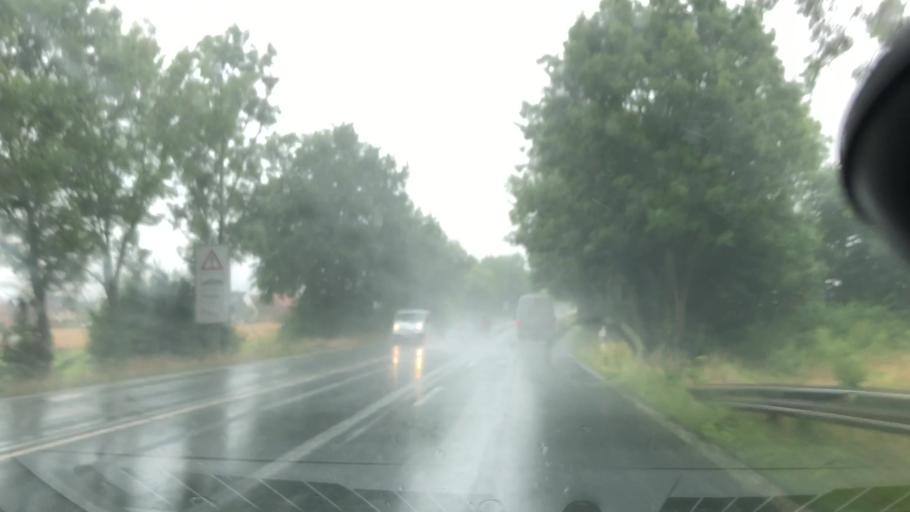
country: DE
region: North Rhine-Westphalia
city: Porta Westfalica
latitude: 52.2163
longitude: 8.8773
